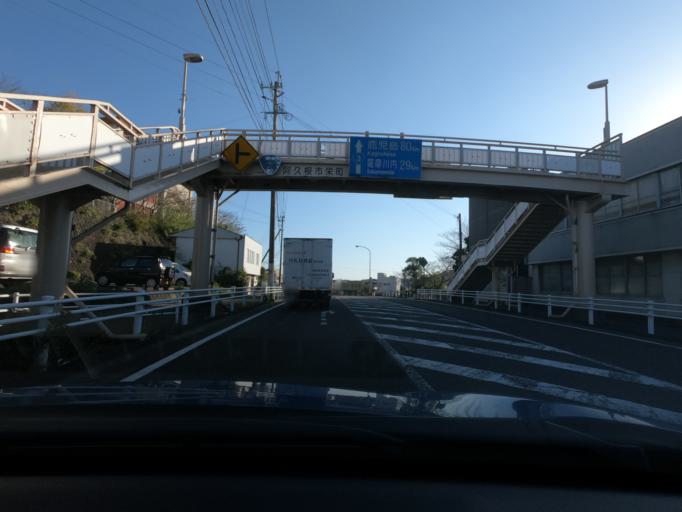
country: JP
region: Kagoshima
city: Akune
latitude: 32.0197
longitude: 130.1958
